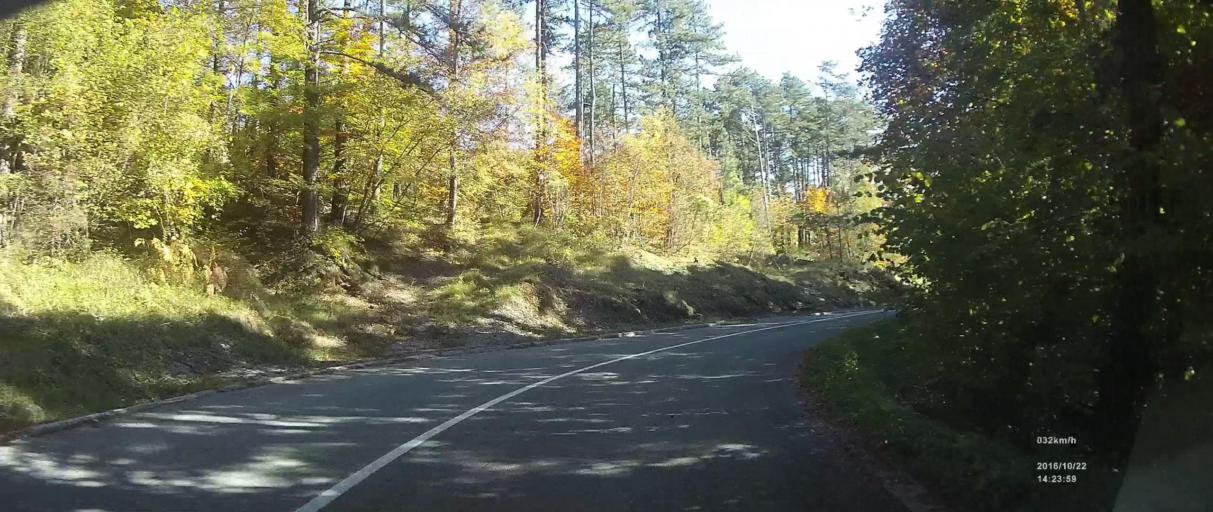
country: HR
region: Istarska
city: Lovran
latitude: 45.3130
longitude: 14.2242
